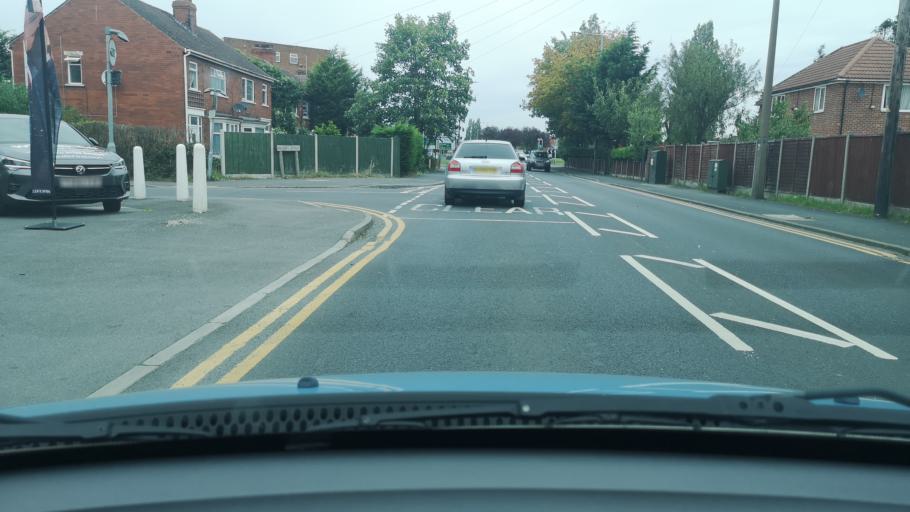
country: GB
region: England
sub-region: North Lincolnshire
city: Scunthorpe
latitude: 53.5887
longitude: -0.6839
